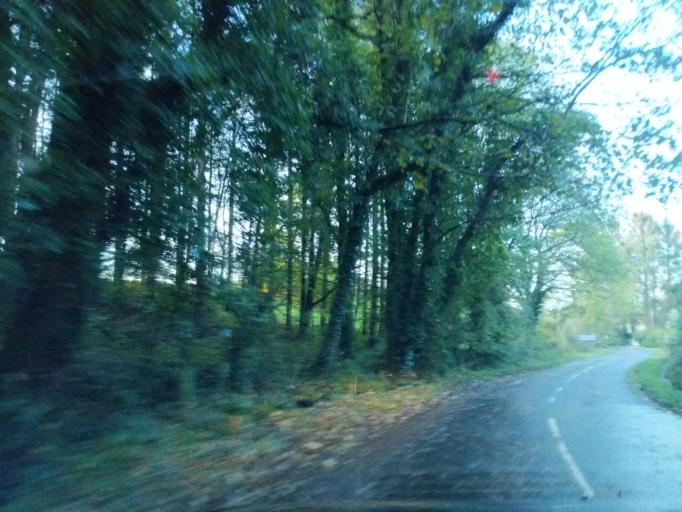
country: GB
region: Scotland
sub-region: Dumfries and Galloway
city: Kirkcudbright
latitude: 54.8357
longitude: -4.0408
